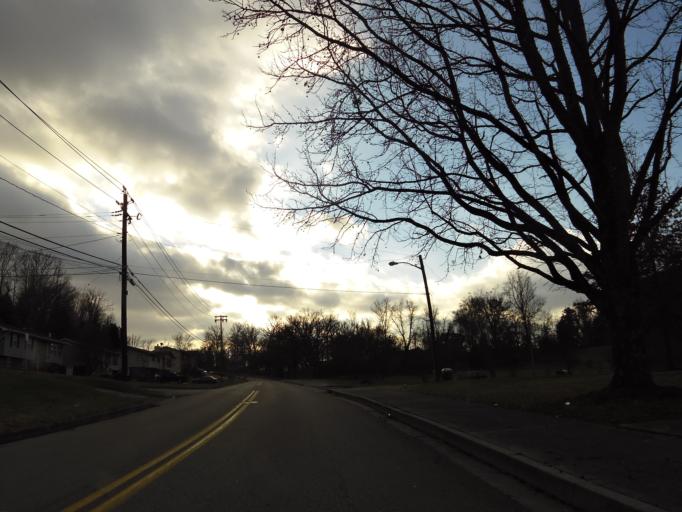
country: US
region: Tennessee
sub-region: Knox County
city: Knoxville
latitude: 35.9392
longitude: -83.8928
